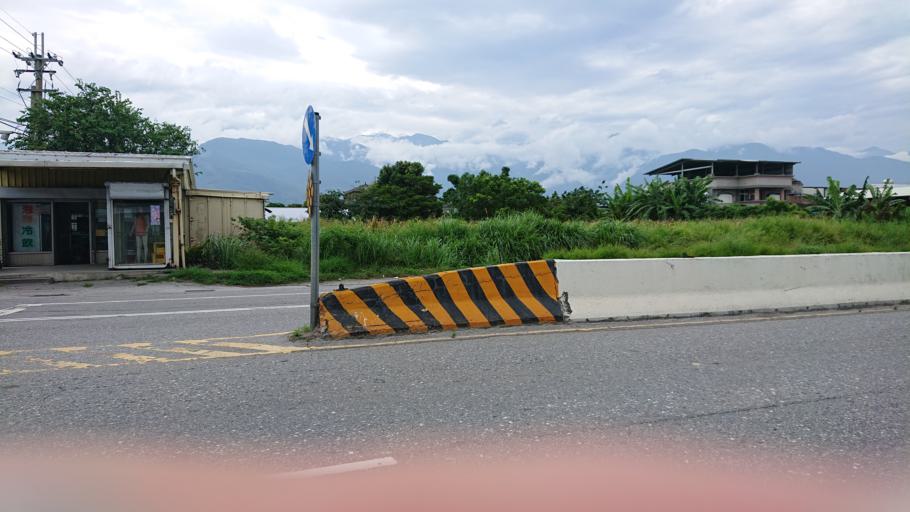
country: TW
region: Taiwan
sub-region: Hualien
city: Hualian
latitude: 23.9480
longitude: 121.5981
